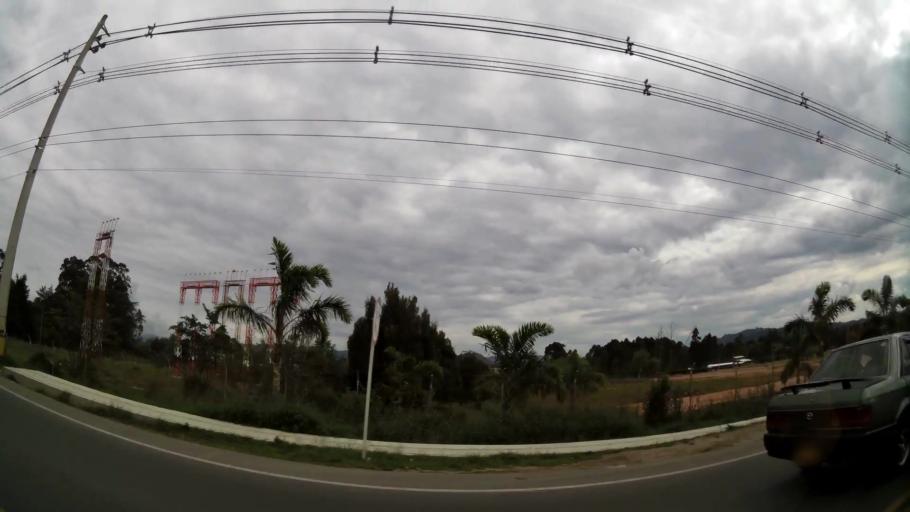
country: CO
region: Antioquia
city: Rionegro
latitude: 6.1472
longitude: -75.4236
